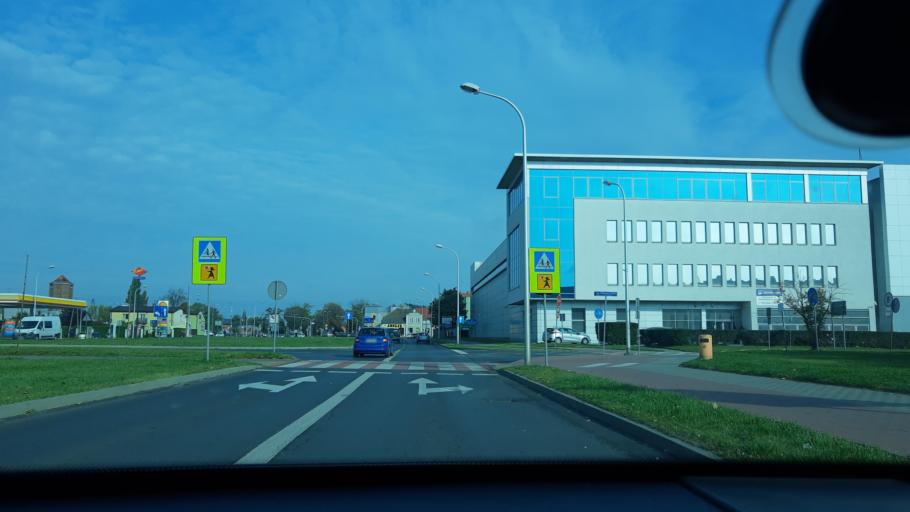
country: PL
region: Lodz Voivodeship
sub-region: Powiat sieradzki
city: Sieradz
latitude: 51.5936
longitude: 18.7152
